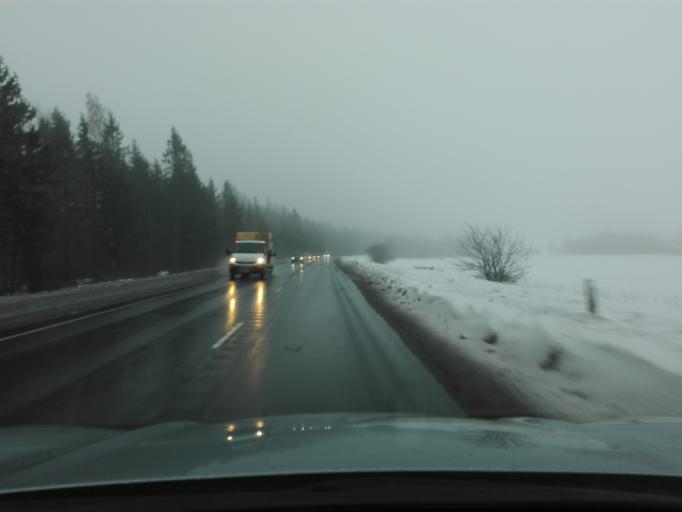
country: EE
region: Raplamaa
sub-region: Kohila vald
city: Kohila
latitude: 59.2302
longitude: 24.7750
